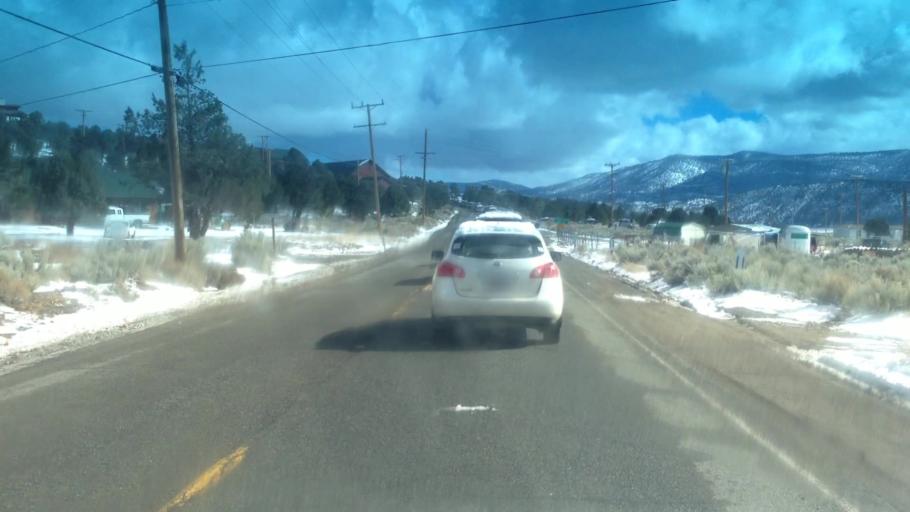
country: US
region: California
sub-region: San Bernardino County
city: Big Bear City
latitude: 34.2920
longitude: -116.8114
